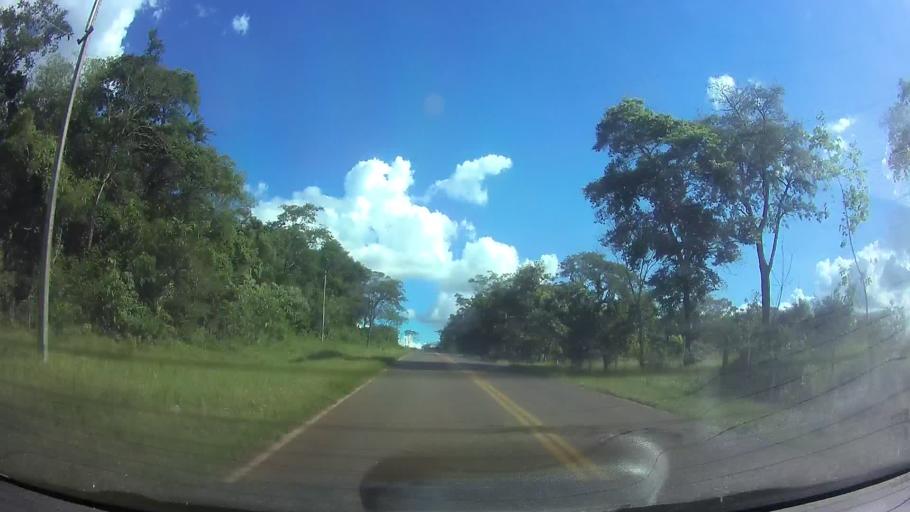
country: PY
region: Paraguari
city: Sapucai
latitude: -25.6439
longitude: -56.8645
